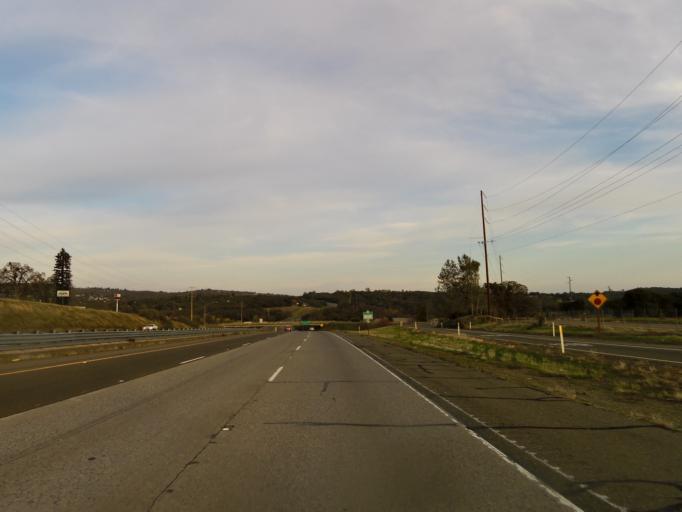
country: US
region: California
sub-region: El Dorado County
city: Cameron Park
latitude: 38.6559
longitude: -121.0025
